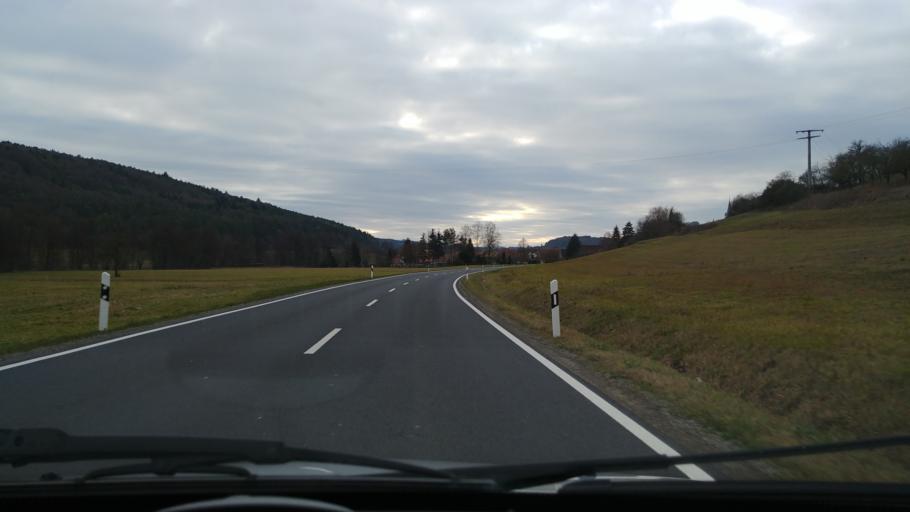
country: DE
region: Bavaria
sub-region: Regierungsbezirk Unterfranken
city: Thungen
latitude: 49.9634
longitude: 9.9041
